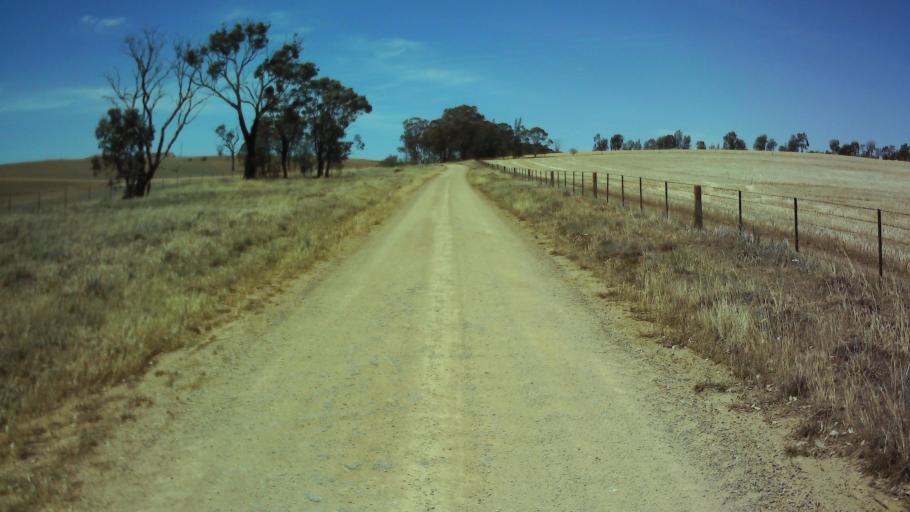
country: AU
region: New South Wales
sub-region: Weddin
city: Grenfell
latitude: -33.9290
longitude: 148.1685
